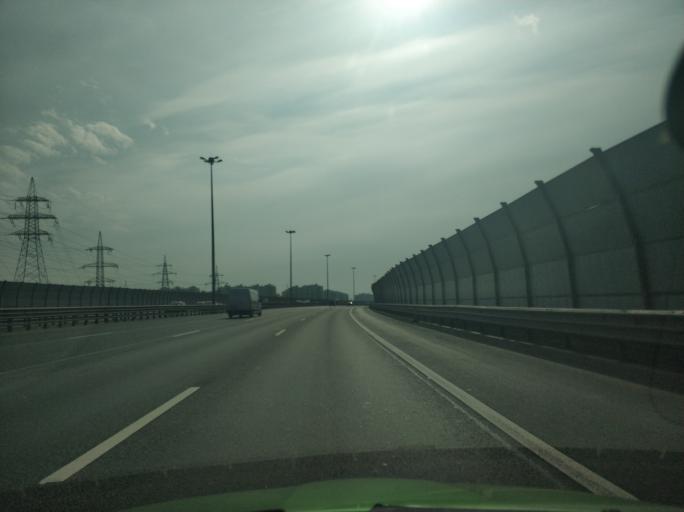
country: RU
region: Leningrad
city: Murino
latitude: 60.0429
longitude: 30.4365
